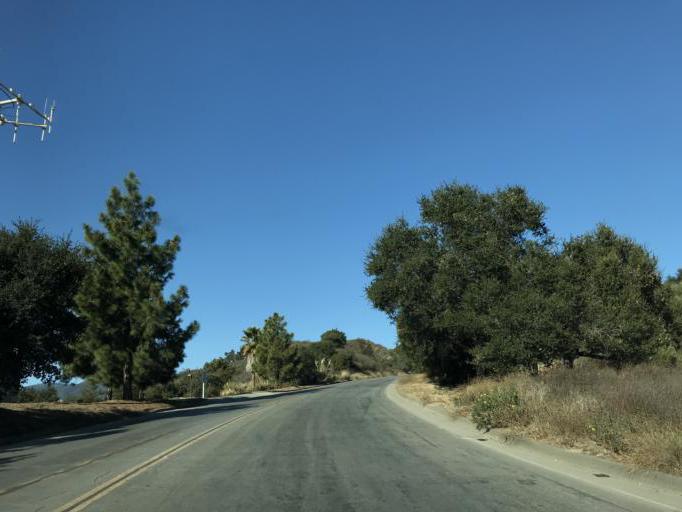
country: US
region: California
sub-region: Santa Barbara County
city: Goleta
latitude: 34.4439
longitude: -119.7759
